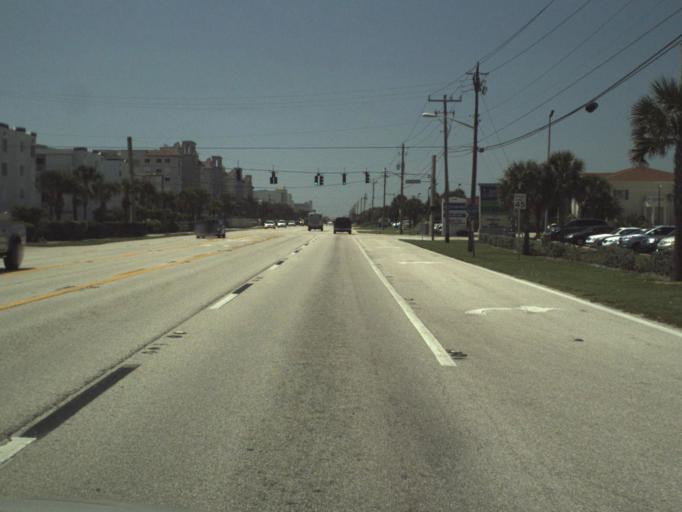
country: US
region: Florida
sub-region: Brevard County
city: Indian Harbour Beach
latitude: 28.1495
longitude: -80.5838
